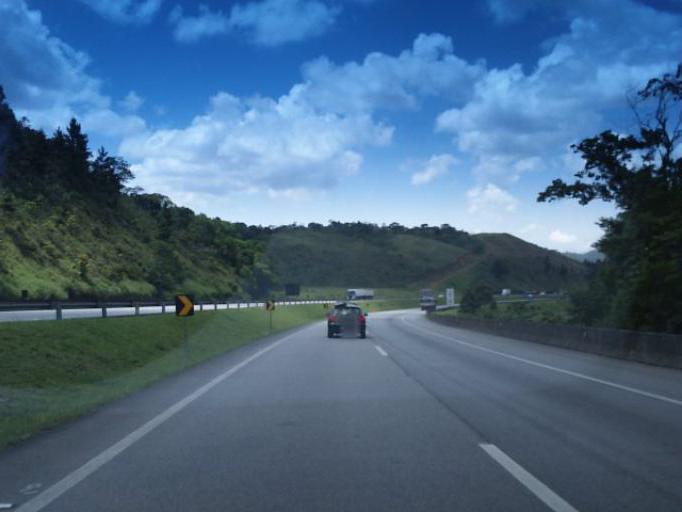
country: BR
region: Sao Paulo
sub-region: Juquitiba
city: Juquitiba
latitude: -23.9924
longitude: -47.1476
